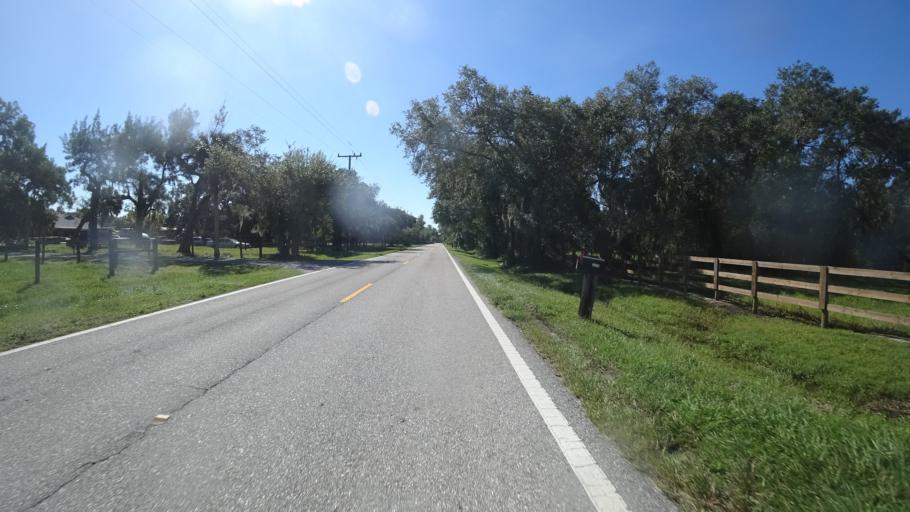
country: US
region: Florida
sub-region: Sarasota County
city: Lake Sarasota
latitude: 27.3098
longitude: -82.2670
